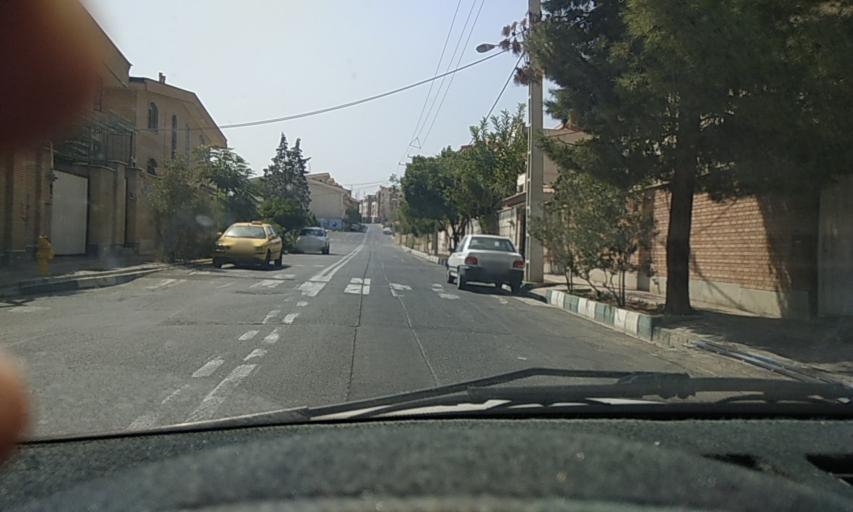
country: IR
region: Tehran
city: Shahr-e Qods
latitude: 35.7544
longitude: 51.1536
